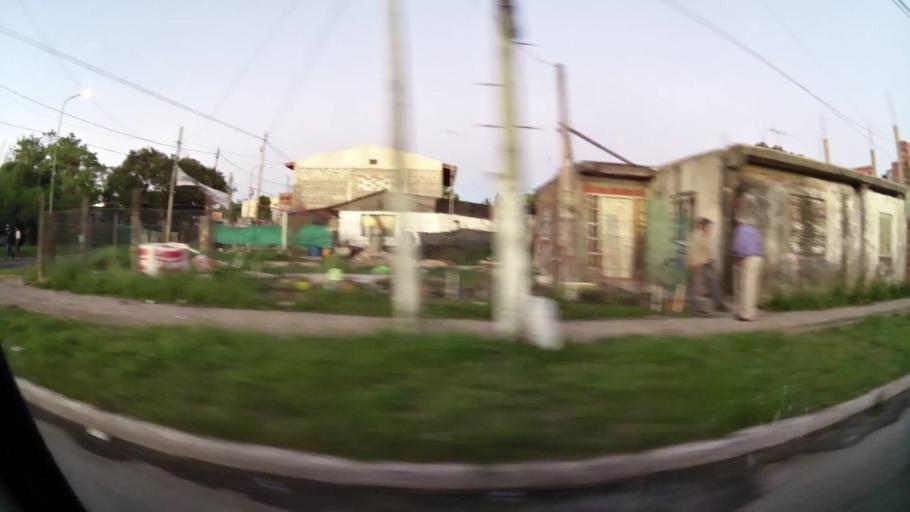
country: AR
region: Buenos Aires
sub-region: Partido de Quilmes
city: Quilmes
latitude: -34.7967
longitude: -58.1731
